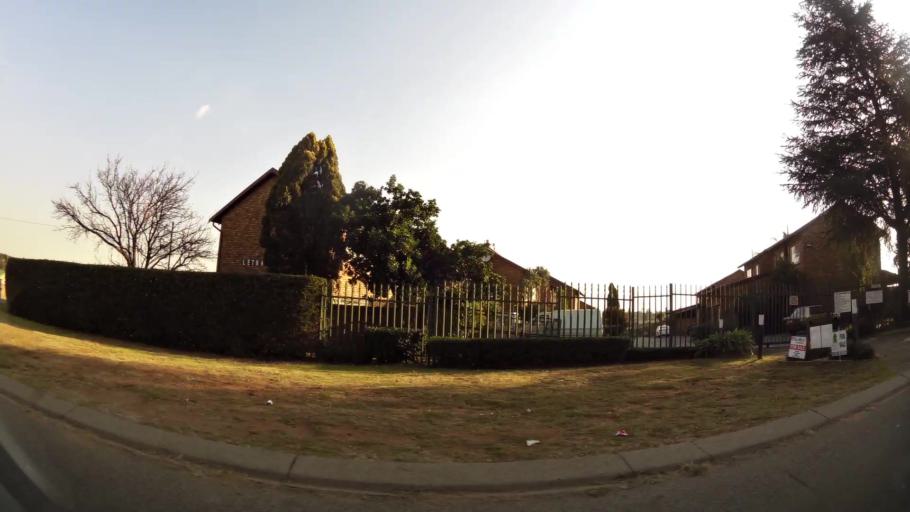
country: ZA
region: Gauteng
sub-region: City of Johannesburg Metropolitan Municipality
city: Modderfontein
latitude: -26.0696
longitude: 28.2226
